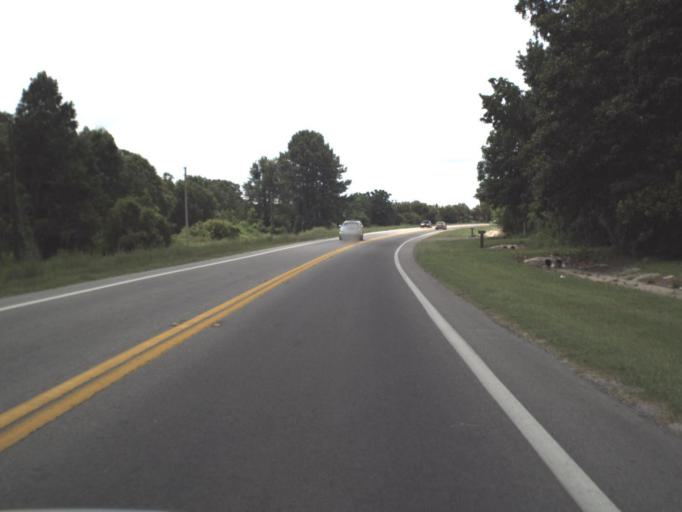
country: US
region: Florida
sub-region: Hamilton County
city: Jasper
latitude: 30.4963
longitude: -82.9333
